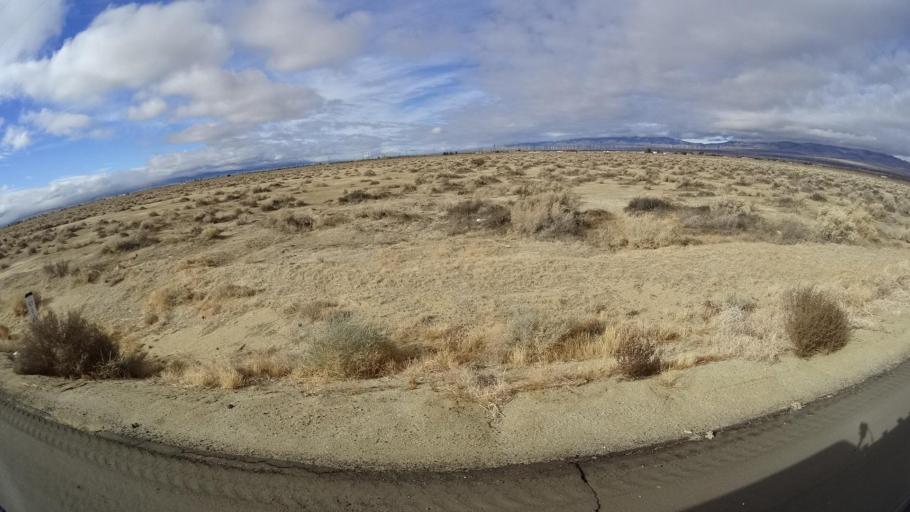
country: US
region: California
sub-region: Kern County
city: Rosamond
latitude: 34.8545
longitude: -118.2909
